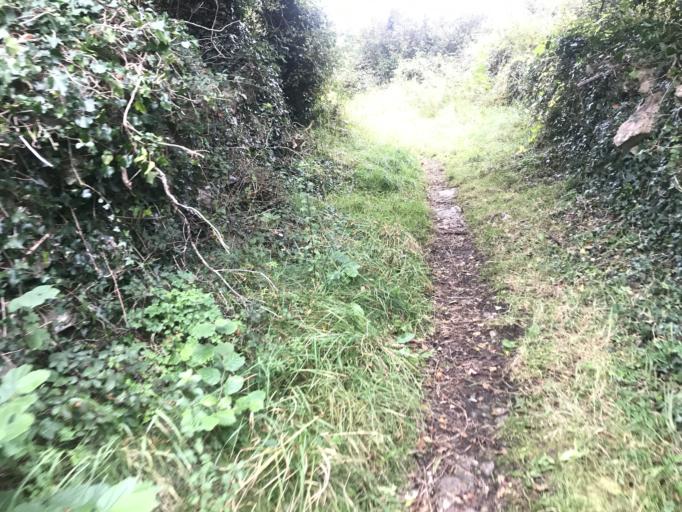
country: IE
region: Connaught
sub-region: County Galway
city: Gaillimh
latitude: 53.2963
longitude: -9.0467
